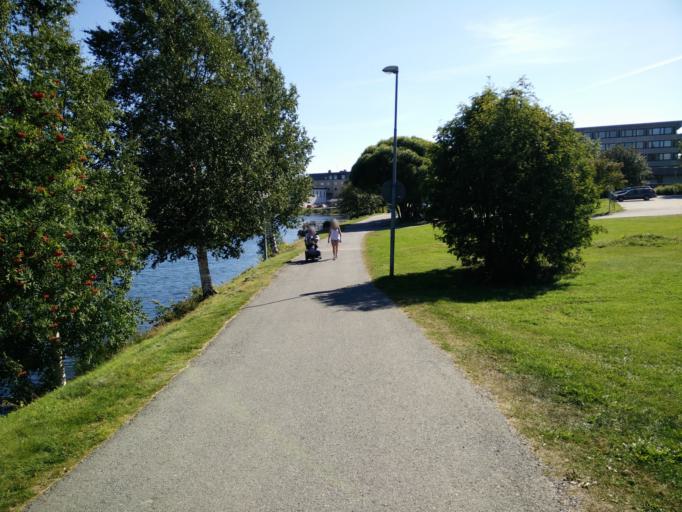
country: SE
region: Vaesternorrland
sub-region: Haernoesands Kommun
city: Haernoesand
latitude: 62.6314
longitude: 17.9306
